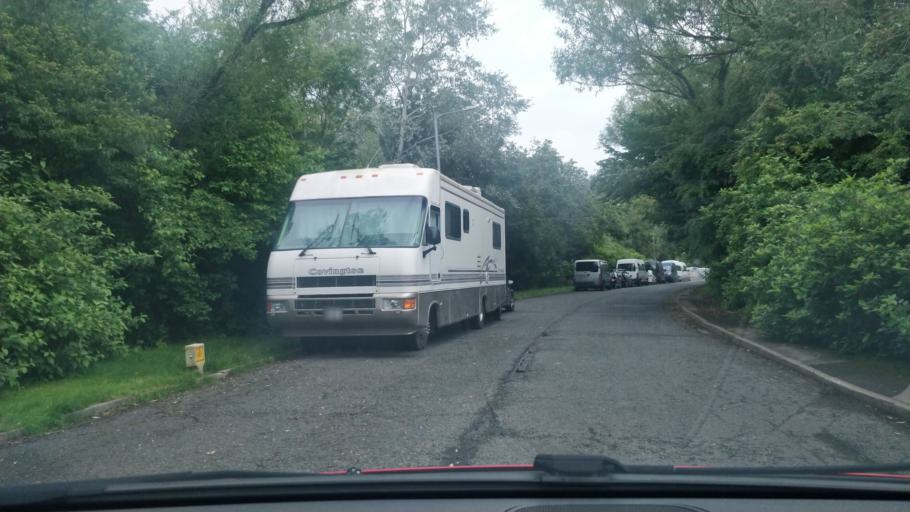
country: GB
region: England
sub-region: Lancashire
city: Leyland
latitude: 53.6981
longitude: -2.7291
